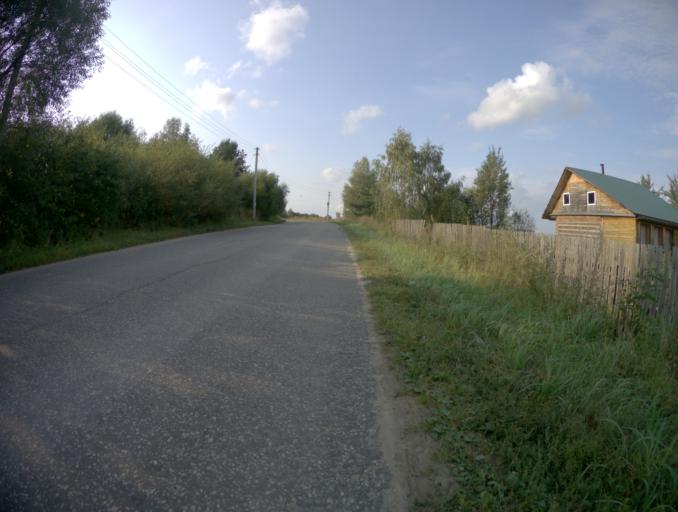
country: RU
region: Vladimir
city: Bogolyubovo
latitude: 56.1131
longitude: 40.5339
